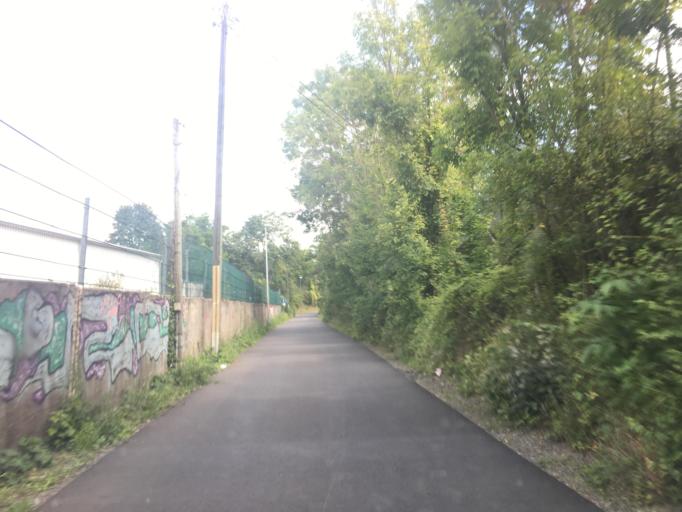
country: DE
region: North Rhine-Westphalia
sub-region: Regierungsbezirk Koln
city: Neustadt/Sued
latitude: 50.9009
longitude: 6.9279
